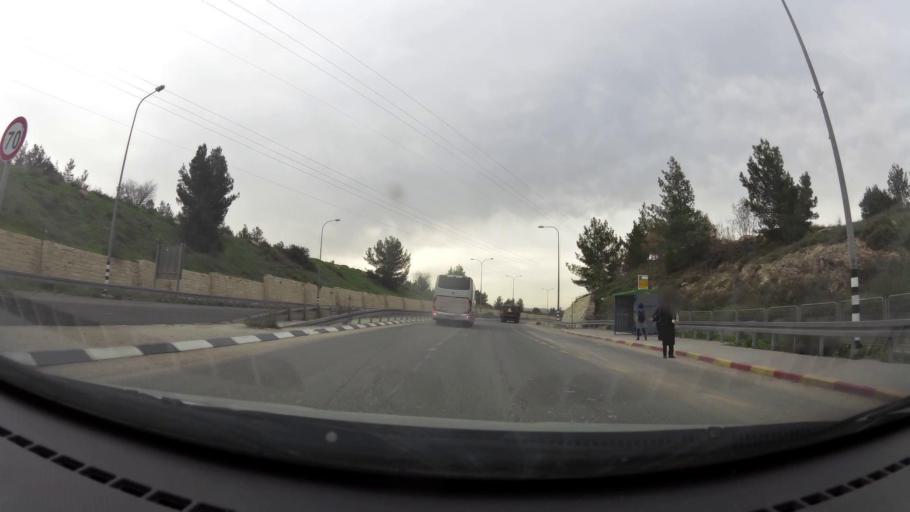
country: IL
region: Jerusalem
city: Bet Shemesh
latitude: 31.6998
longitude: 35.0090
